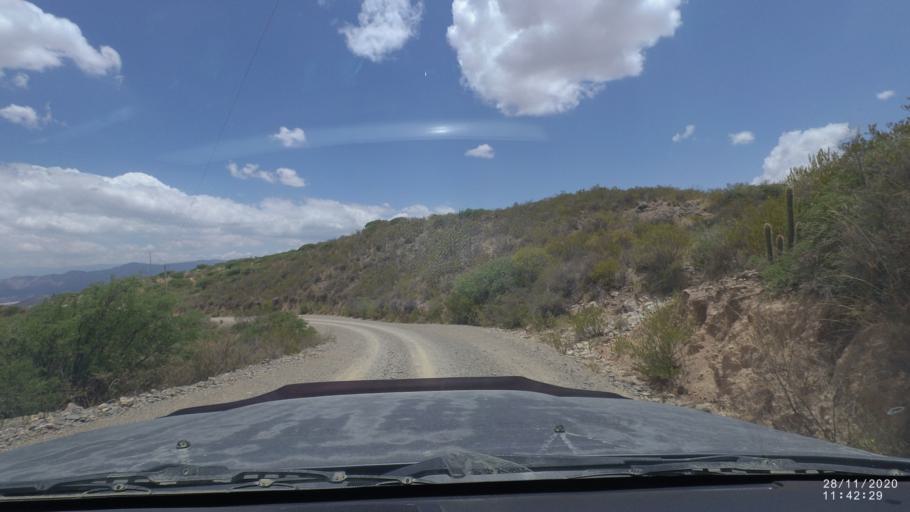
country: BO
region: Cochabamba
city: Tarata
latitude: -17.6645
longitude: -66.0465
